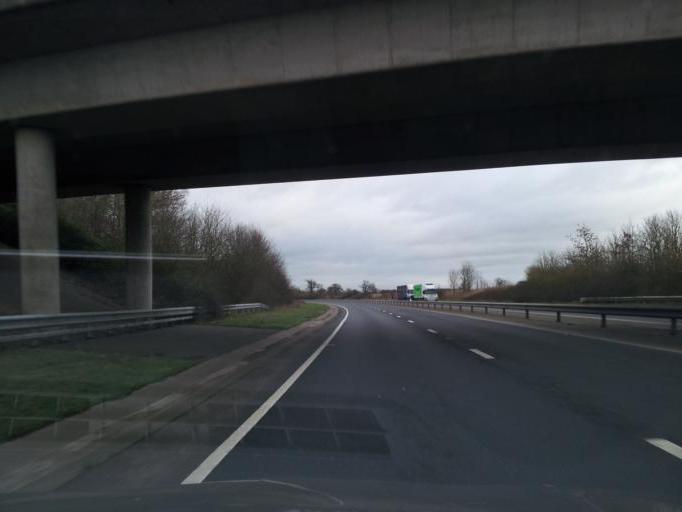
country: GB
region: England
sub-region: Norfolk
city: Diss
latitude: 52.3803
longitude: 1.1739
